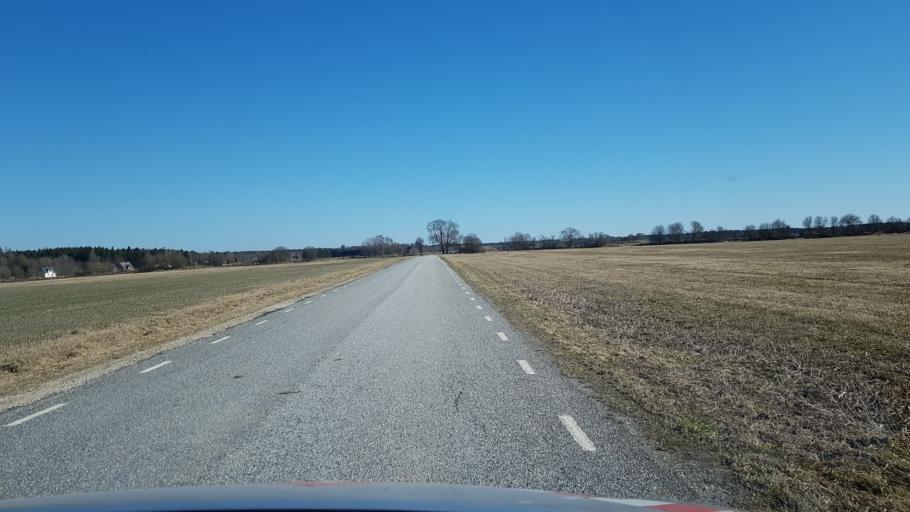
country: EE
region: Laeaene-Virumaa
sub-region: Viru-Nigula vald
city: Kunda
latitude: 59.4044
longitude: 26.5413
